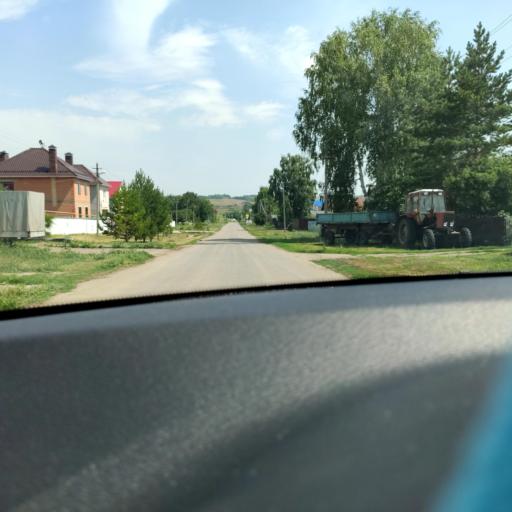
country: RU
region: Samara
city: Petra-Dubrava
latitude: 53.3419
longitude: 50.5186
